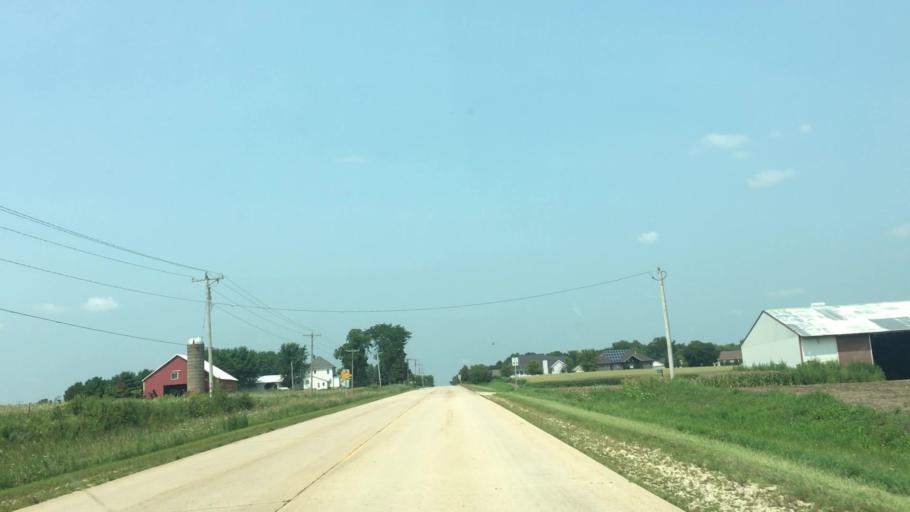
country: US
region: Iowa
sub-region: Fayette County
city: Oelwein
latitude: 42.6718
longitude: -91.8938
